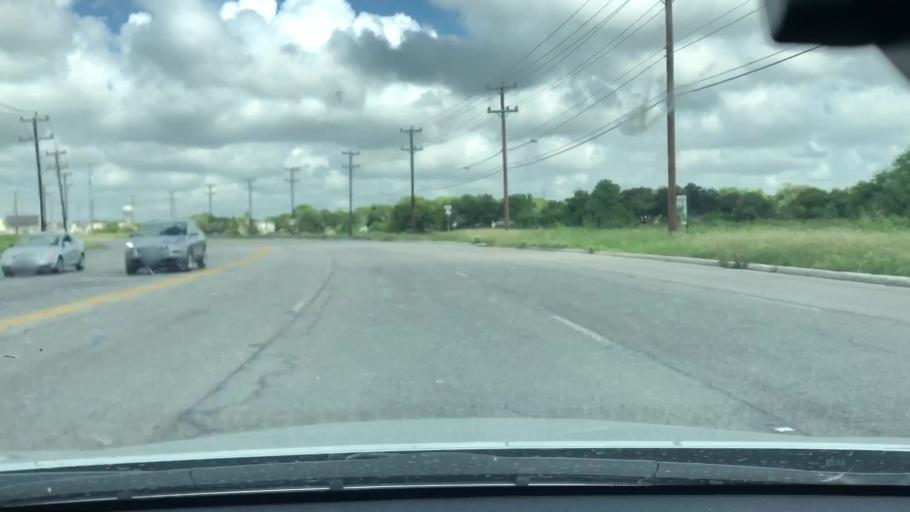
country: US
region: Texas
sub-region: Bexar County
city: Windcrest
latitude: 29.5038
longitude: -98.3677
